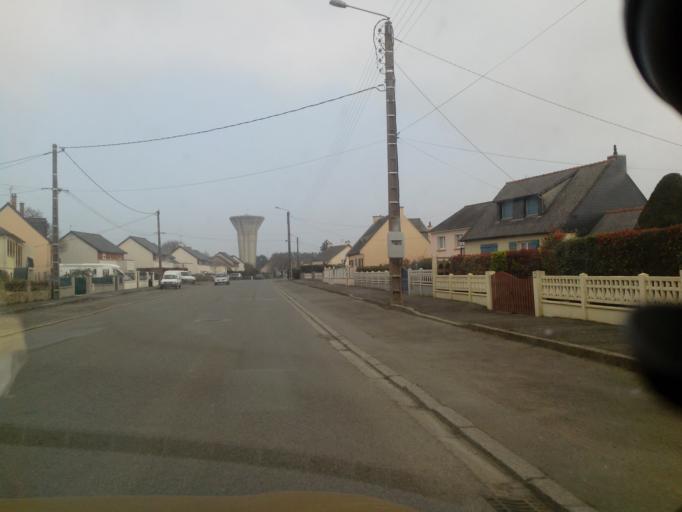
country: FR
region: Brittany
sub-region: Departement d'Ille-et-Vilaine
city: Saint-Meen-le-Grand
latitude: 48.1935
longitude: -2.1874
